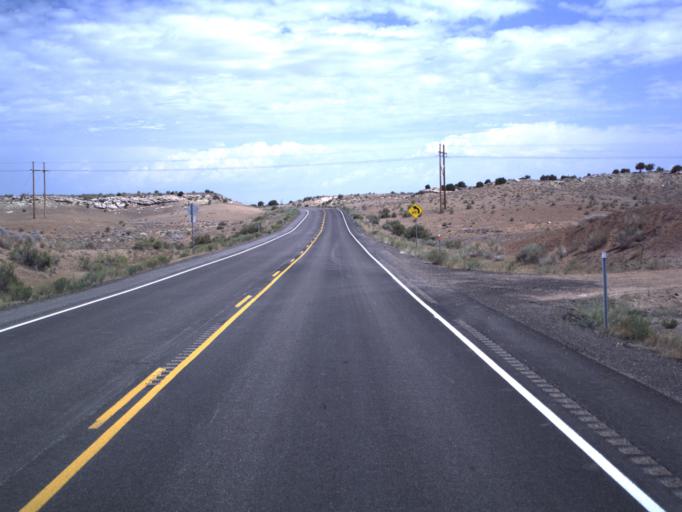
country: US
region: Utah
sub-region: Uintah County
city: Naples
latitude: 40.1889
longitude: -109.3310
